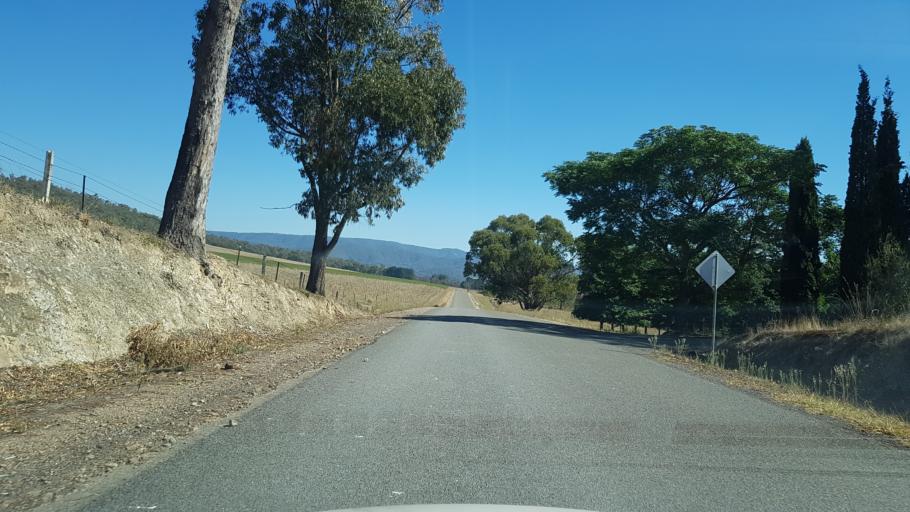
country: AU
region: Victoria
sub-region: Mansfield
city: Mansfield
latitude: -36.8202
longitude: 146.4818
